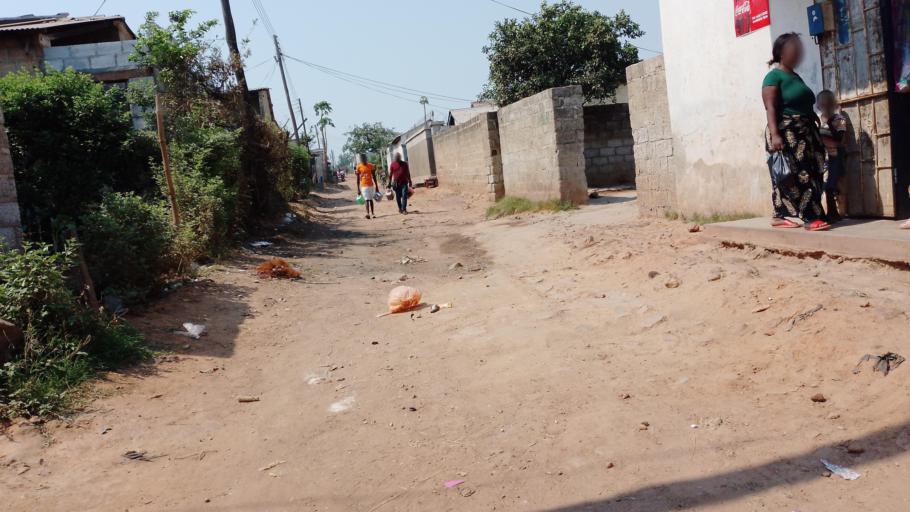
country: ZM
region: Lusaka
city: Lusaka
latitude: -15.3971
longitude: 28.3694
